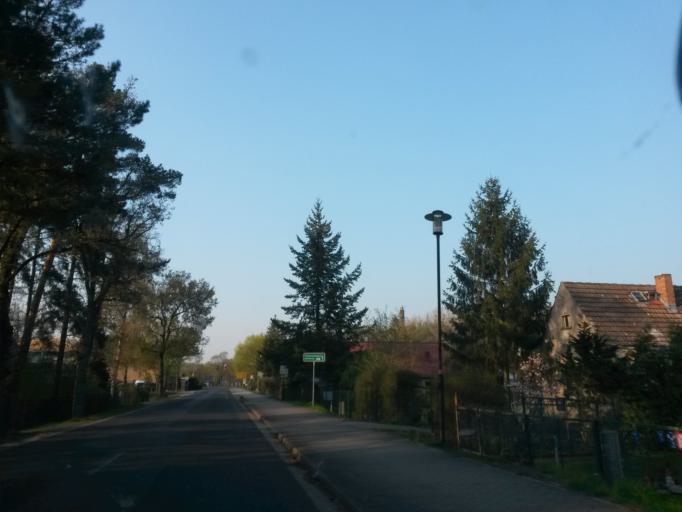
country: DE
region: Brandenburg
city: Rehfelde
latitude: 52.4791
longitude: 13.9106
